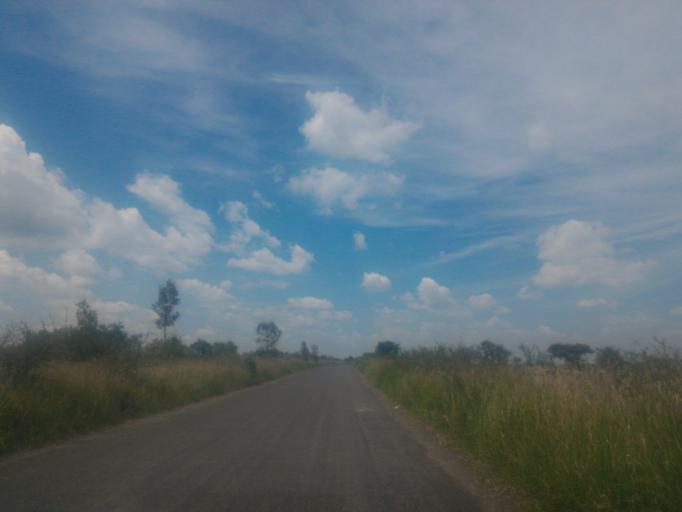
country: MX
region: Guanajuato
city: Ciudad Manuel Doblado
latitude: 20.8113
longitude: -102.0680
